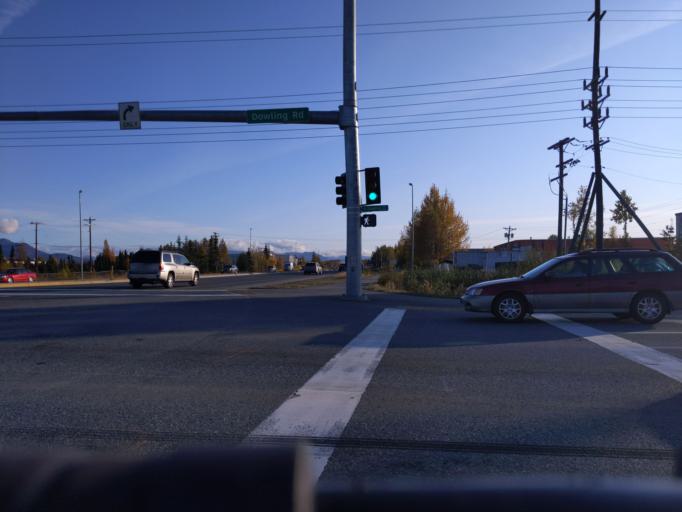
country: US
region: Alaska
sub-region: Anchorage Municipality
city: Anchorage
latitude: 61.1667
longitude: -149.8871
